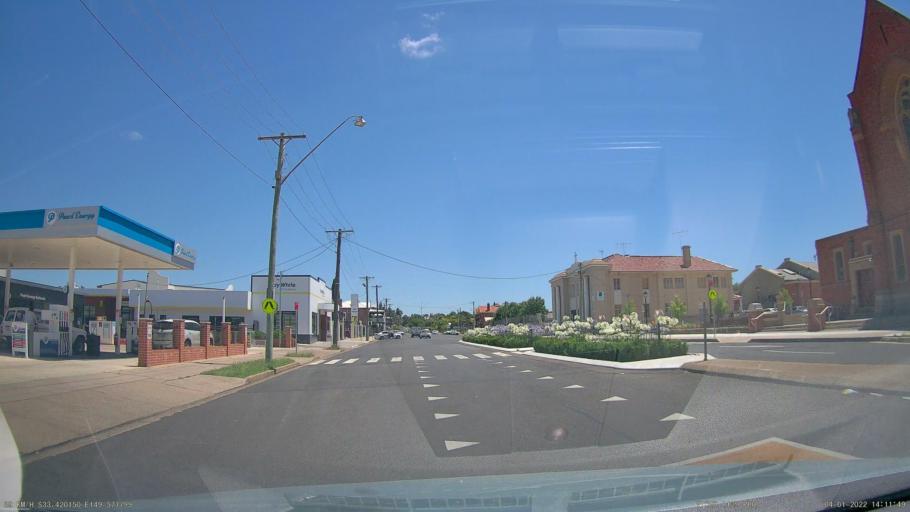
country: AU
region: New South Wales
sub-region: Bathurst Regional
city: Bathurst
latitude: -33.4202
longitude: 149.5776
